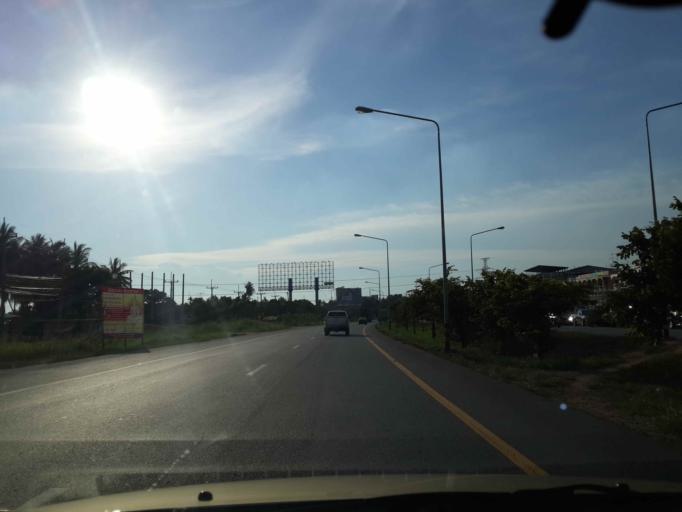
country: TH
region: Chon Buri
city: Bang Lamung
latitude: 12.9918
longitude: 100.9396
